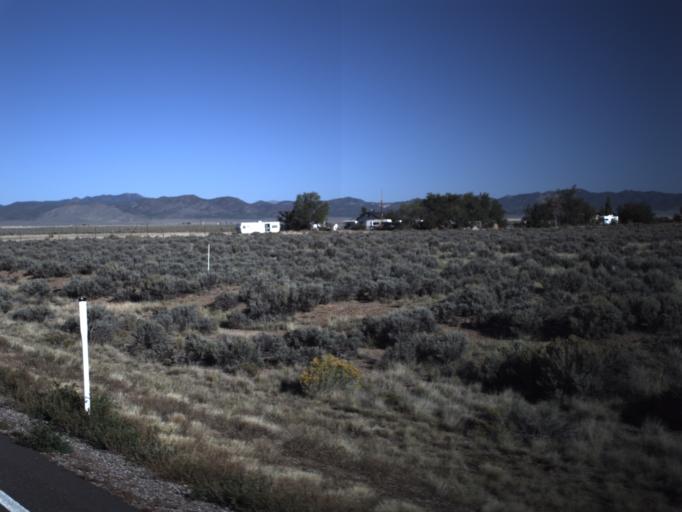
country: US
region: Utah
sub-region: Washington County
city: Enterprise
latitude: 37.7657
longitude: -113.8154
